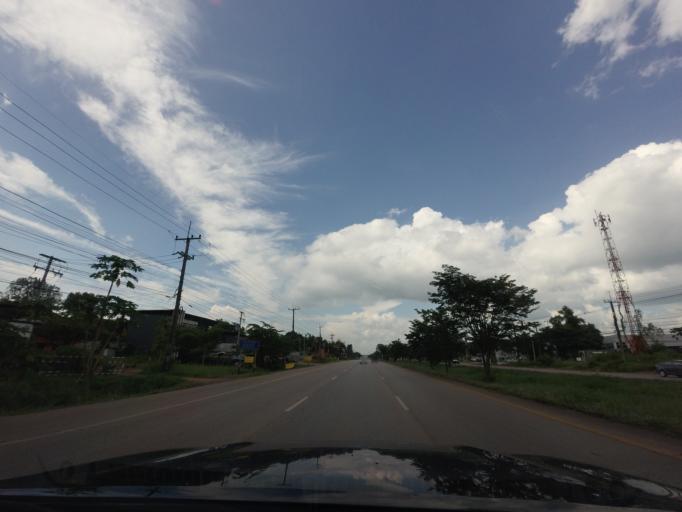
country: TH
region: Changwat Udon Thani
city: Udon Thani
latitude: 17.5390
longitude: 102.8001
